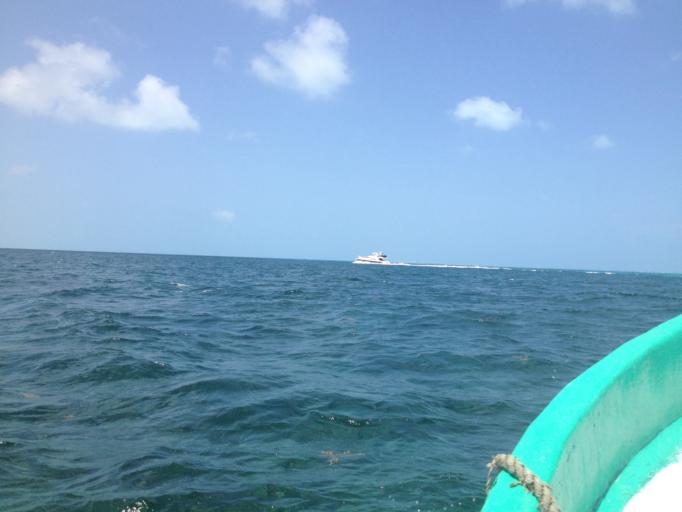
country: MX
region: Quintana Roo
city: Cancun
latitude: 21.1942
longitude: -86.7989
